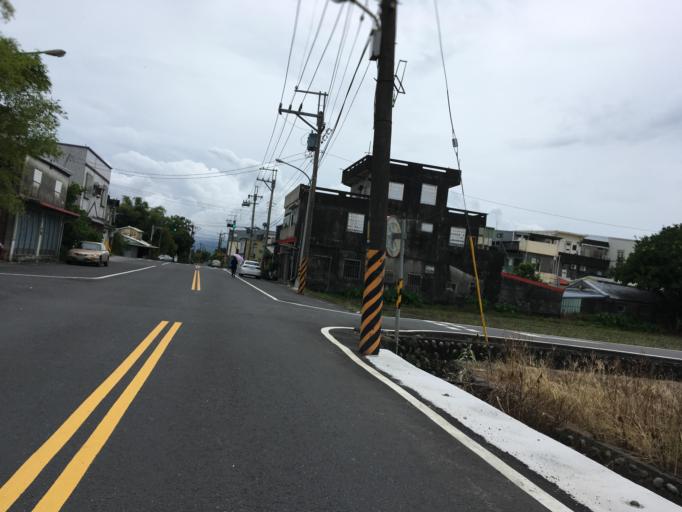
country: TW
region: Taiwan
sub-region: Yilan
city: Yilan
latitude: 24.6953
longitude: 121.8109
